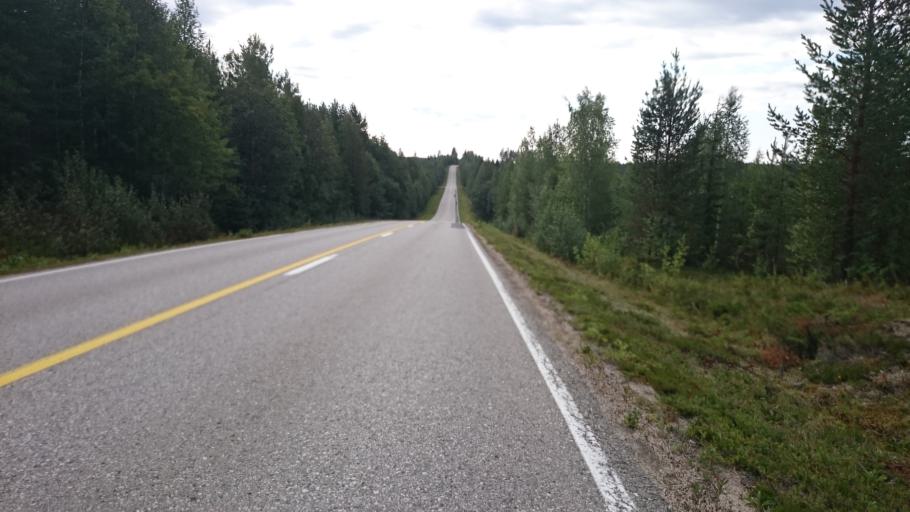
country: FI
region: Kainuu
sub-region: Kehys-Kainuu
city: Kuhmo
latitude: 64.4292
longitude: 29.8124
